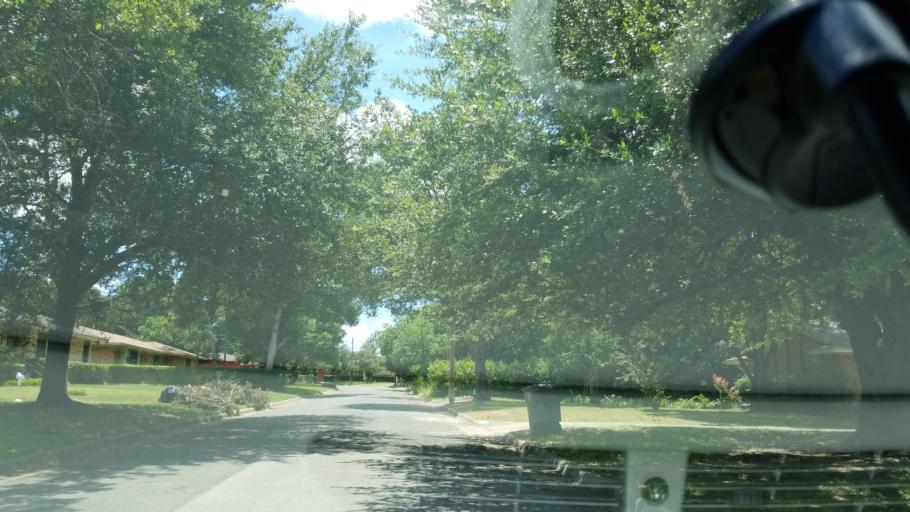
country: US
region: Texas
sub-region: Dallas County
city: Cockrell Hill
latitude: 32.7025
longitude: -96.8764
